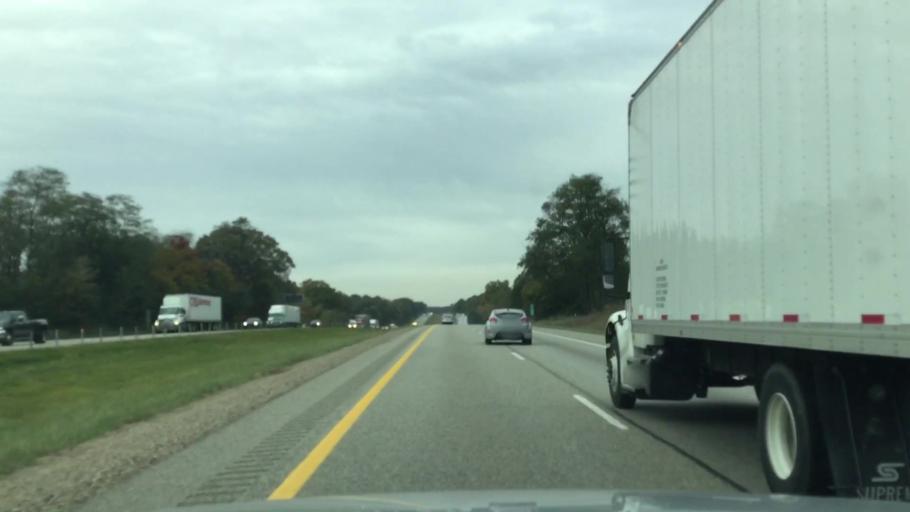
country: US
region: Michigan
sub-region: Kalamazoo County
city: Galesburg
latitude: 42.2777
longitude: -85.3224
